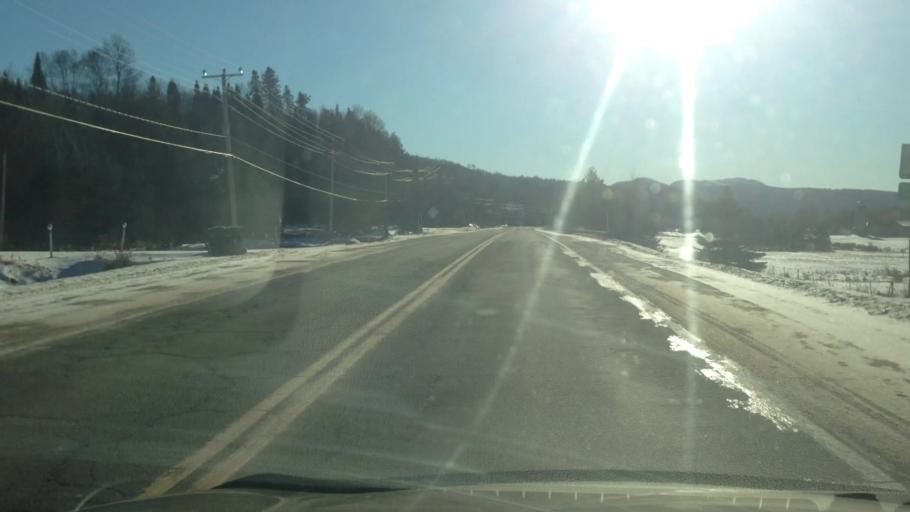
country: CA
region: Quebec
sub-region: Laurentides
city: Mont-Tremblant
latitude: 46.0853
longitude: -74.6114
